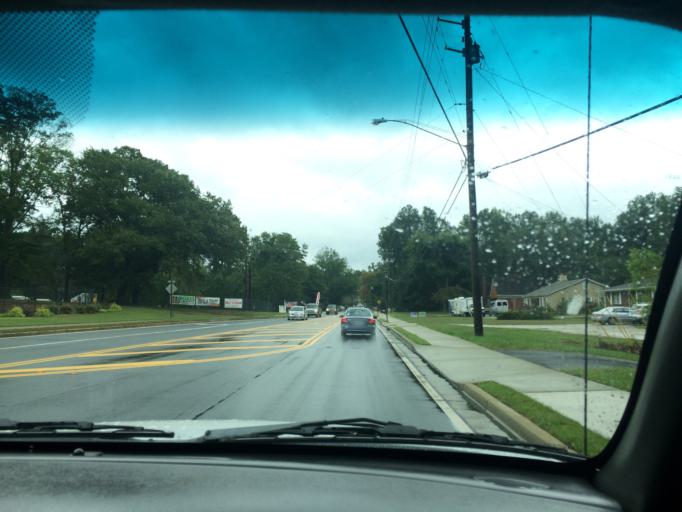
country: US
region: Georgia
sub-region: Cobb County
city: Kennesaw
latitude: 34.0287
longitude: -84.6257
